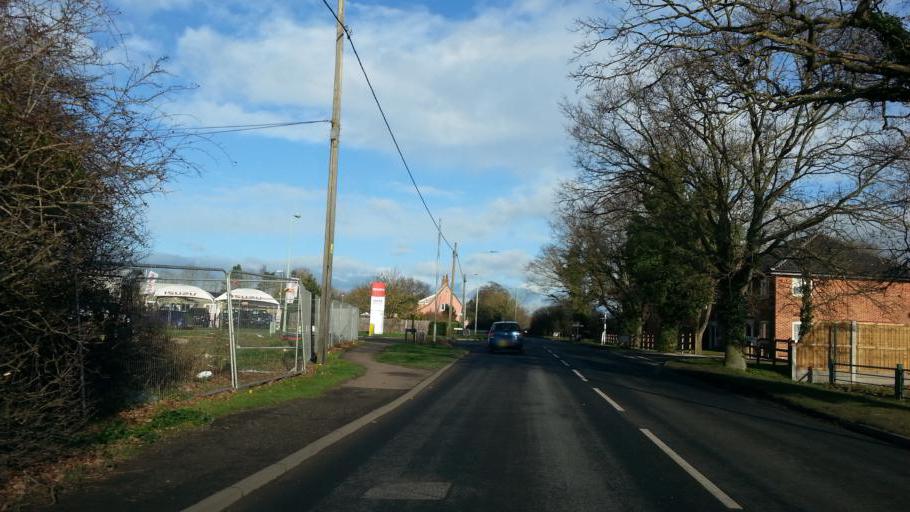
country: GB
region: England
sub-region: Suffolk
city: Halesworth
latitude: 52.3526
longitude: 1.5100
